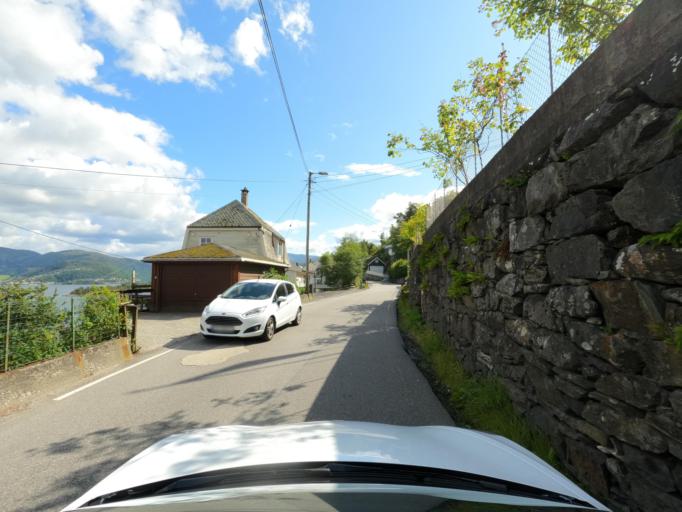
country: NO
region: Hordaland
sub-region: Bergen
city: Ytre Arna
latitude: 60.4569
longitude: 5.4414
